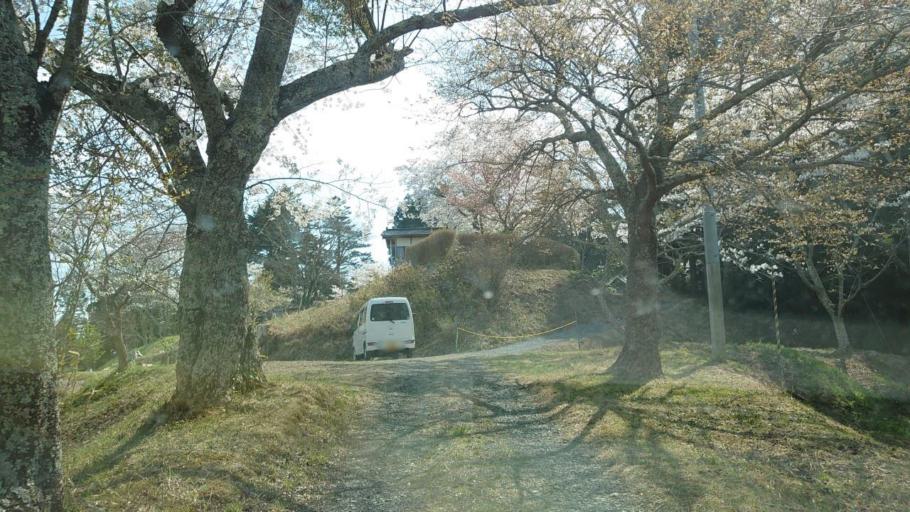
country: JP
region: Iwate
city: Ichinoseki
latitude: 38.8494
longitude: 141.1589
